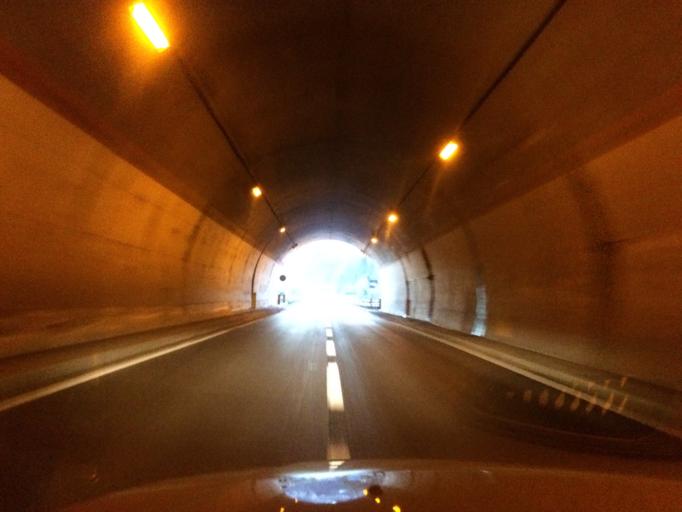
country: IT
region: Emilia-Romagna
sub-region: Forli-Cesena
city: Sarsina
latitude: 43.9239
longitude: 12.1657
